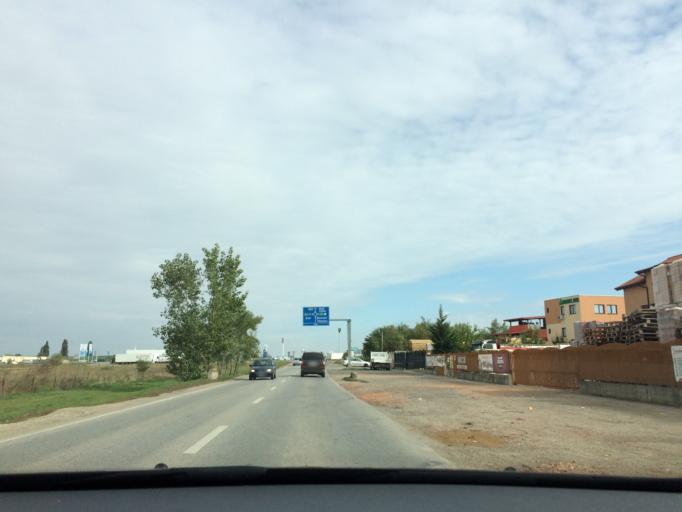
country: RO
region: Timis
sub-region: Comuna Dumbravita
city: Dumbravita
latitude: 45.8110
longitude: 21.2598
